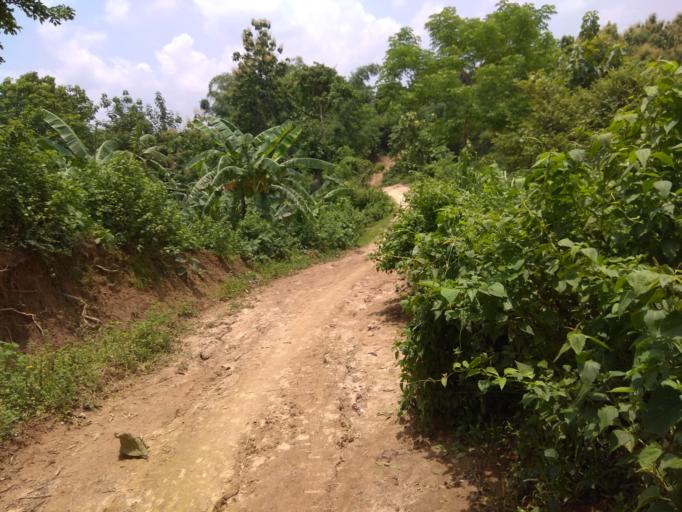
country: BD
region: Chittagong
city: Manikchari
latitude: 22.8851
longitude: 91.9276
